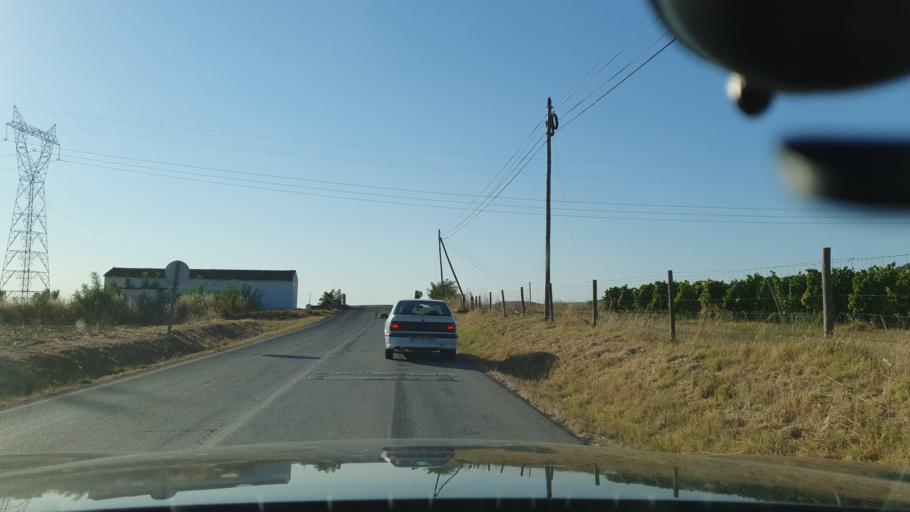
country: PT
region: Evora
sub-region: Estremoz
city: Estremoz
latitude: 38.8669
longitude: -7.6250
